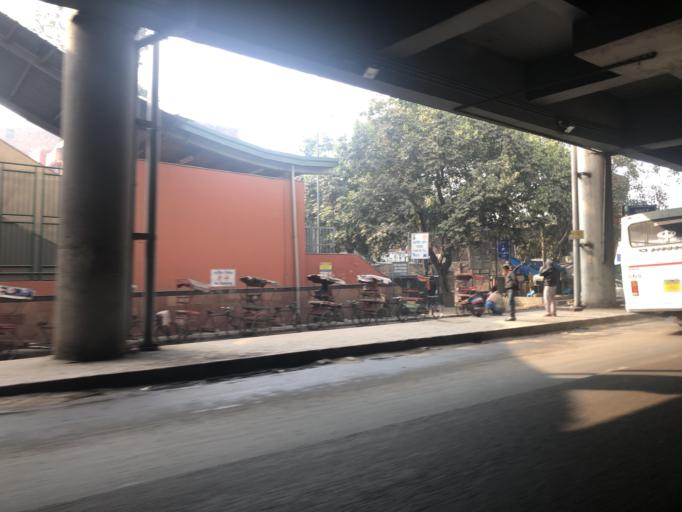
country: IN
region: NCT
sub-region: North West Delhi
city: Pitampura
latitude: 28.6748
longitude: 77.1308
